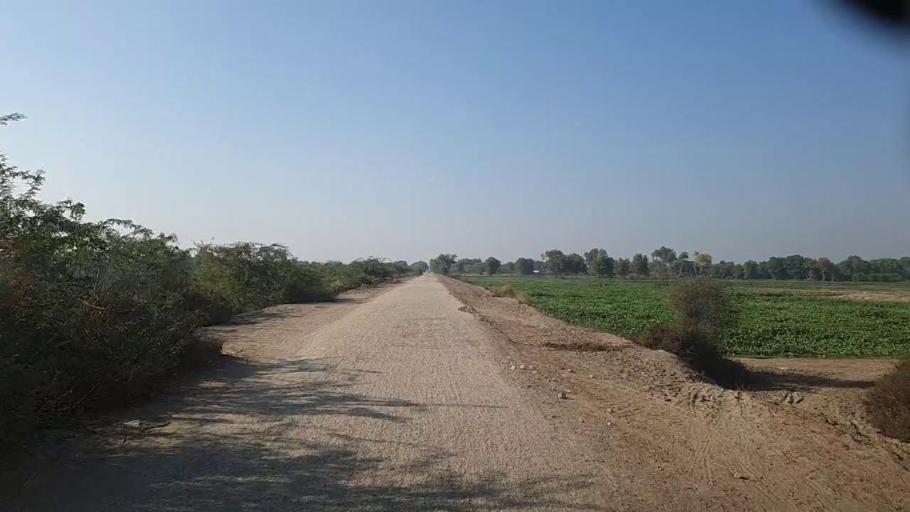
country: PK
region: Sindh
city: Darya Khan Marri
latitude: 26.6717
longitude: 68.3843
